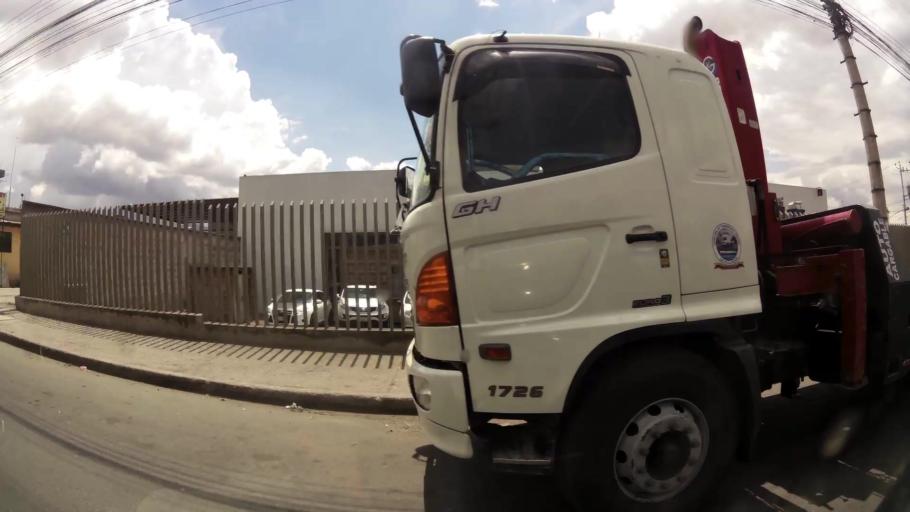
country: EC
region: Pichincha
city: Quito
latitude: -0.1080
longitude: -78.4510
